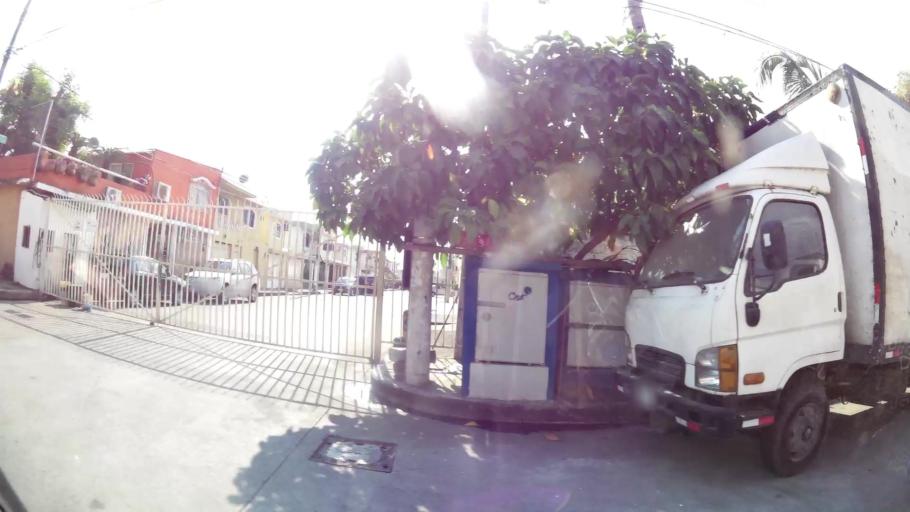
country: EC
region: Guayas
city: Guayaquil
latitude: -2.1320
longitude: -79.9275
